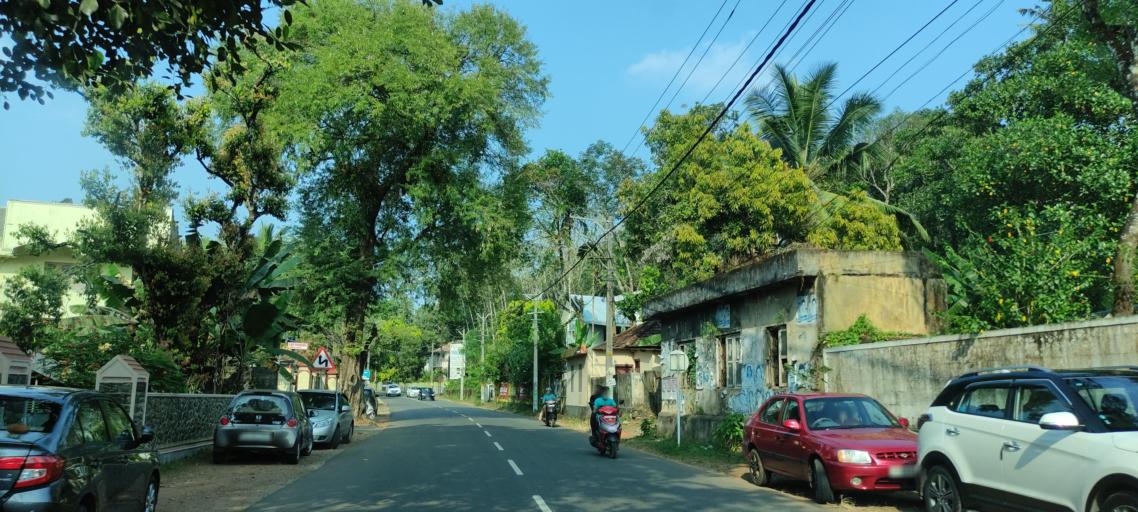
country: IN
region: Kerala
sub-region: Pattanamtitta
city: Adur
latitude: 9.0952
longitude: 76.6884
